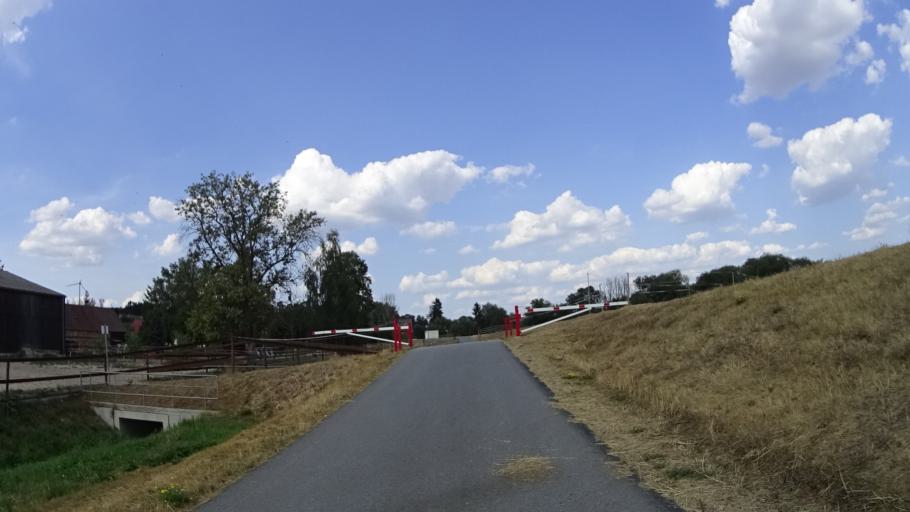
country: DE
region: Saxony
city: Ostritz
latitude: 51.0384
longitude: 14.9464
